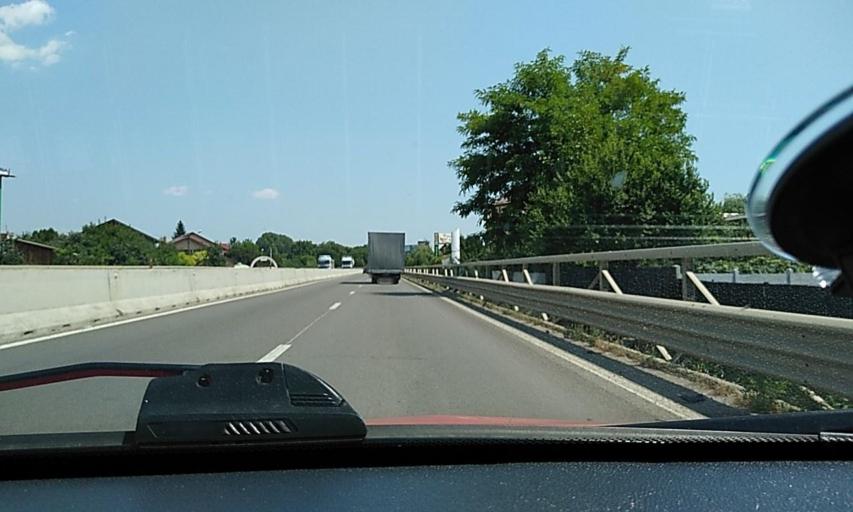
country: RO
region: Prahova
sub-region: Comuna Barcanesti
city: Barcanesti
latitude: 44.8868
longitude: 26.0403
